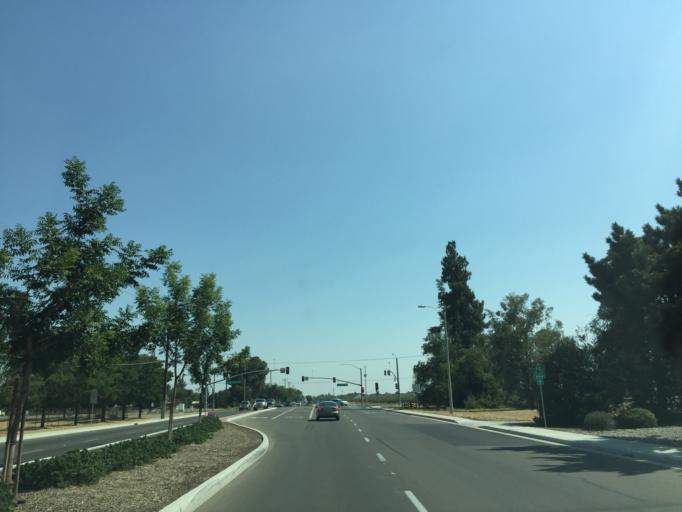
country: US
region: California
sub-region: Kings County
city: Hanford
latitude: 36.3440
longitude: -119.6729
